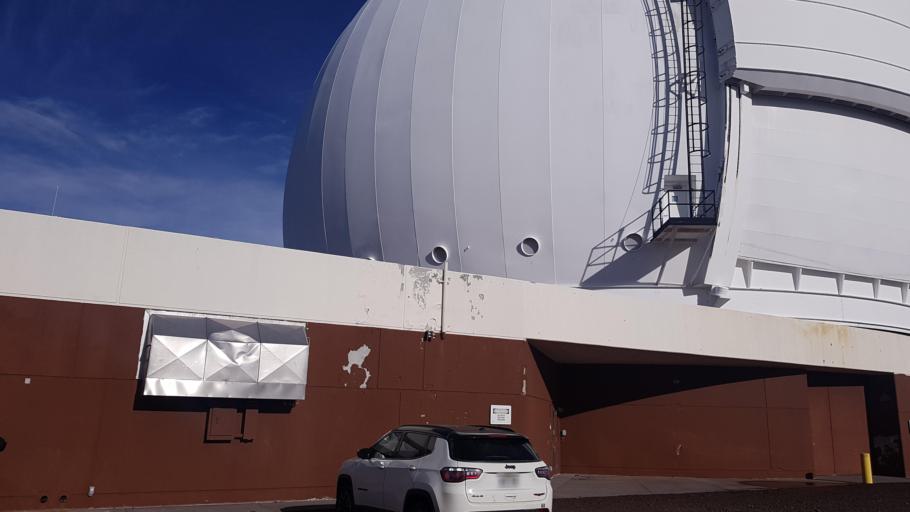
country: US
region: Hawaii
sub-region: Hawaii County
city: Honoka'a
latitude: 19.8262
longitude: -155.4742
